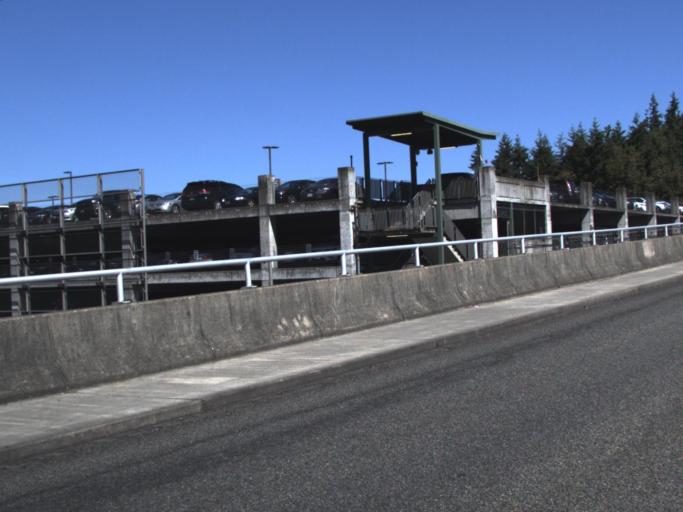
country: US
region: Washington
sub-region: King County
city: Seattle
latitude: 47.5933
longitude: -122.3291
